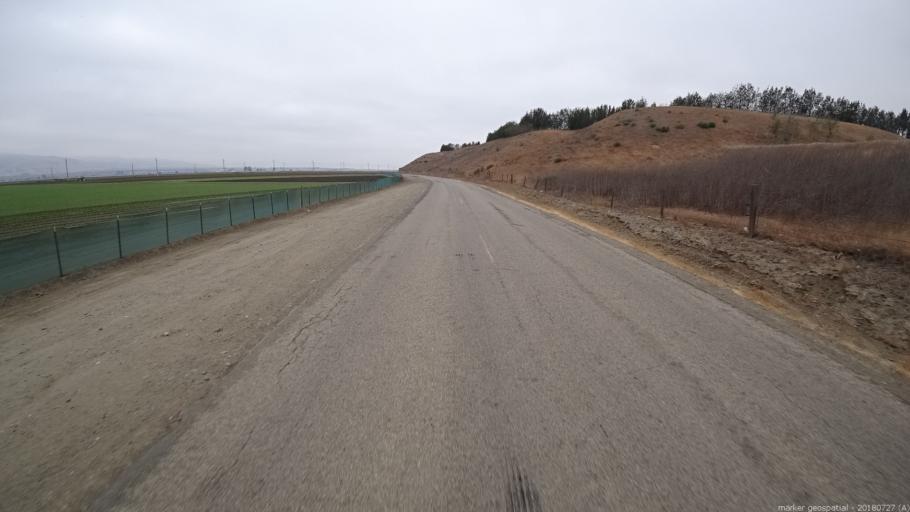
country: US
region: California
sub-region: Monterey County
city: King City
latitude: 36.2403
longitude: -121.1298
